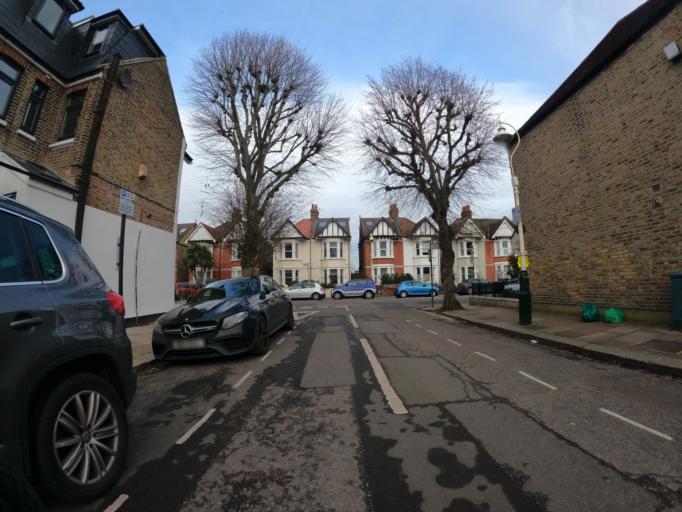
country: GB
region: England
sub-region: Greater London
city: Brentford
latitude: 51.5020
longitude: -0.3198
